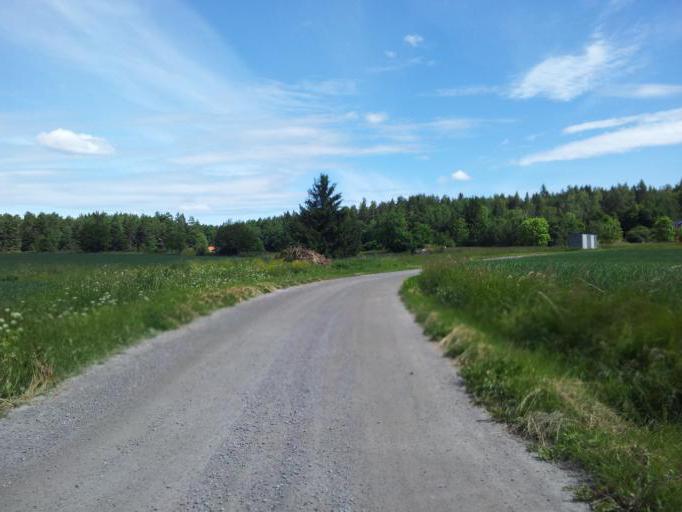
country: SE
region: Uppsala
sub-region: Uppsala Kommun
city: Saevja
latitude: 59.8655
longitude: 17.7368
